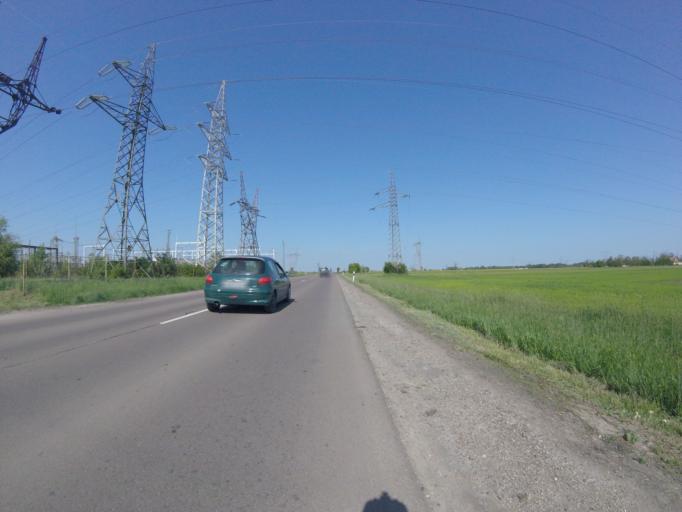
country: HU
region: Jasz-Nagykun-Szolnok
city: Zagyvarekas
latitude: 47.2155
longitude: 20.1374
